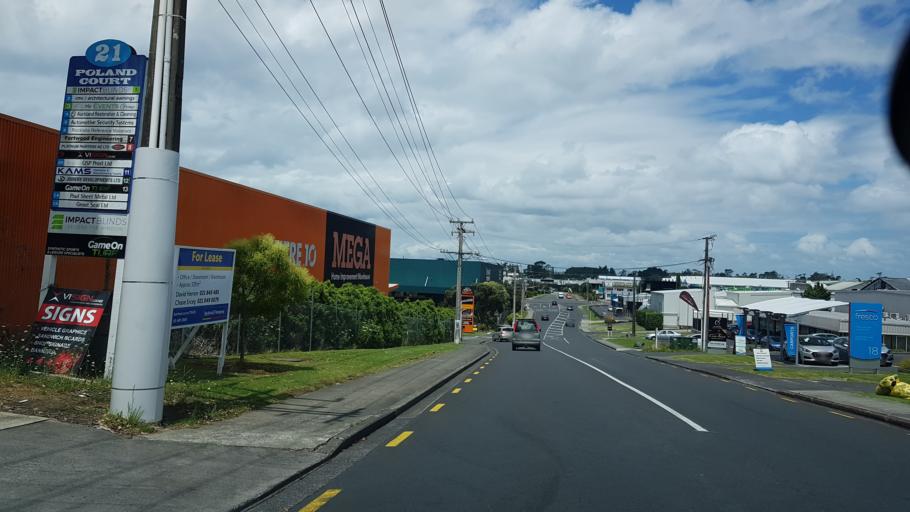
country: NZ
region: Auckland
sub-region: Auckland
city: North Shore
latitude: -36.7765
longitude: 174.7404
